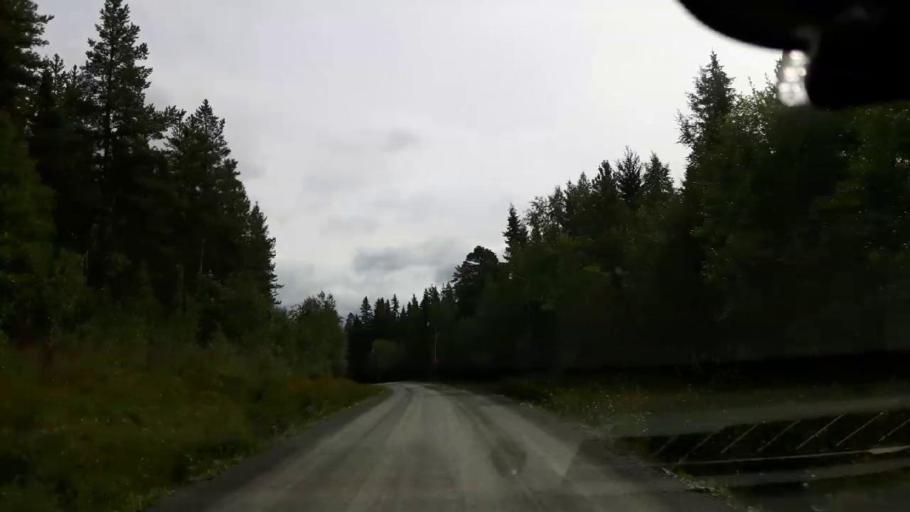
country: SE
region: Jaemtland
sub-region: Krokoms Kommun
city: Valla
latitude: 63.6291
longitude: 14.0215
